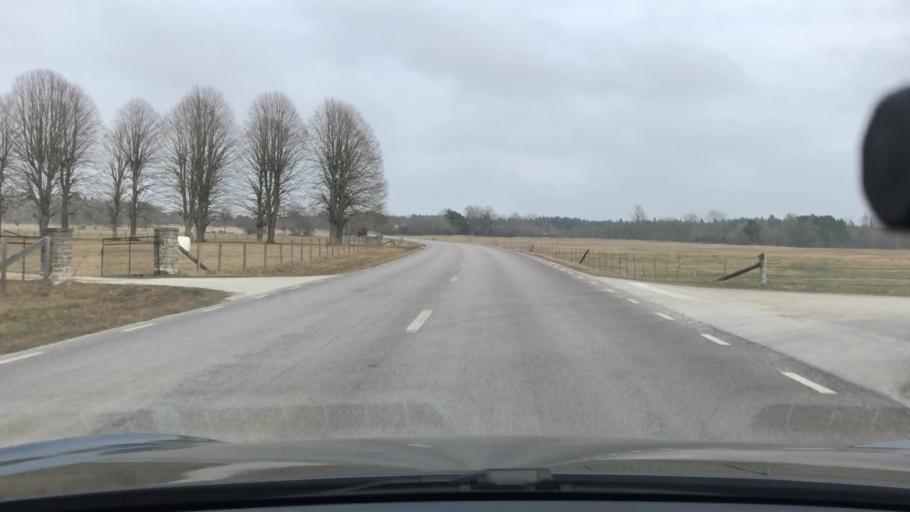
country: SE
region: Gotland
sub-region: Gotland
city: Slite
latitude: 57.4351
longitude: 18.6780
